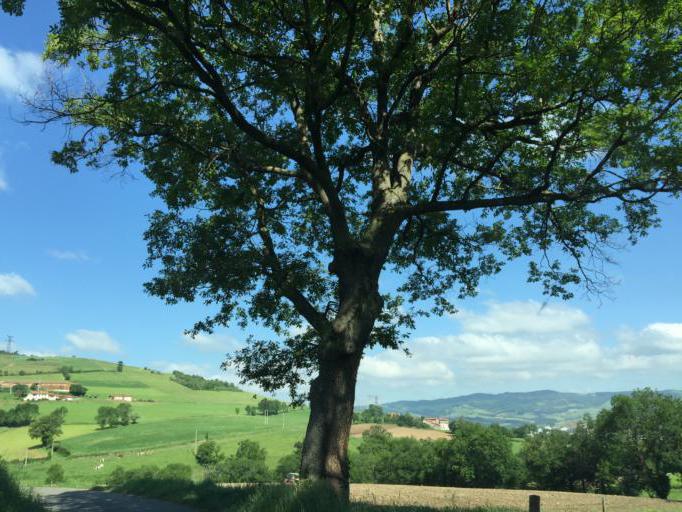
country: FR
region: Rhone-Alpes
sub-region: Departement de la Loire
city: Saint-Chamond
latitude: 45.4541
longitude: 4.5470
